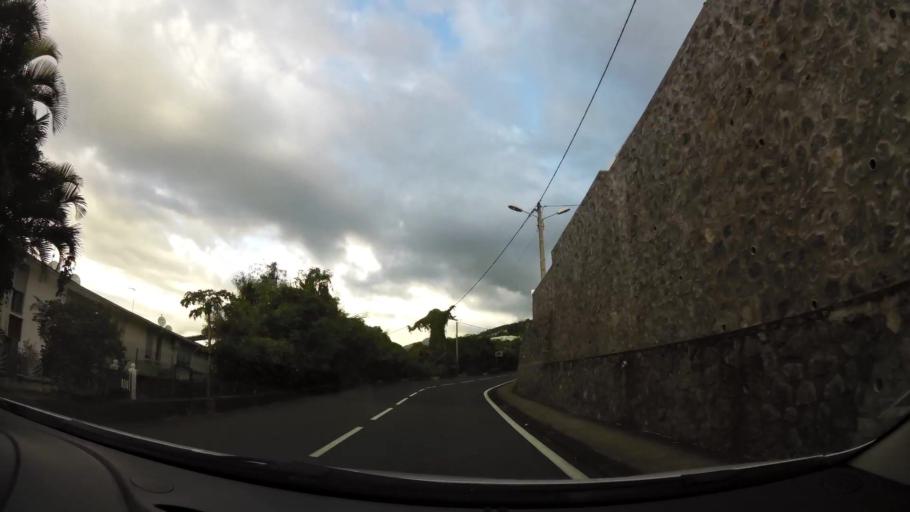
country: RE
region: Reunion
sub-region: Reunion
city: Saint-Denis
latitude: -20.8978
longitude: 55.4440
